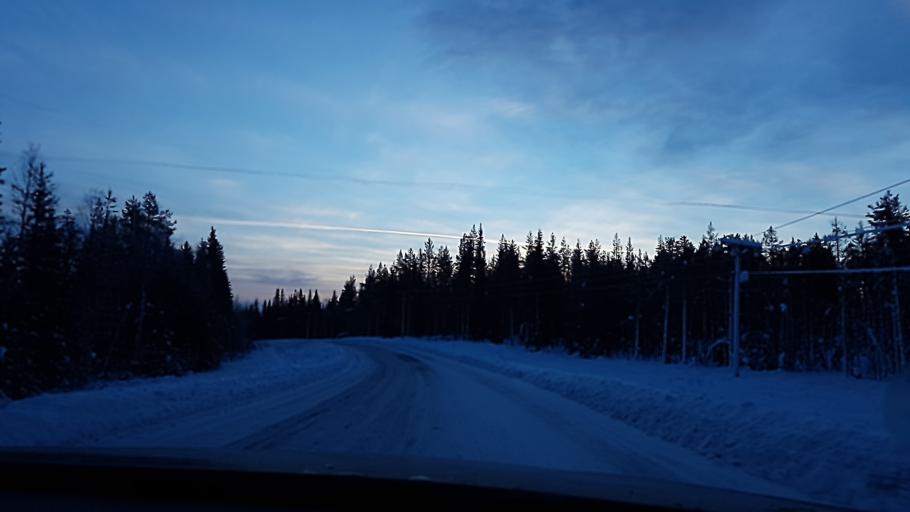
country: SE
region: Norrbotten
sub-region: Jokkmokks Kommun
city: Jokkmokk
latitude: 66.1300
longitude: 20.0034
